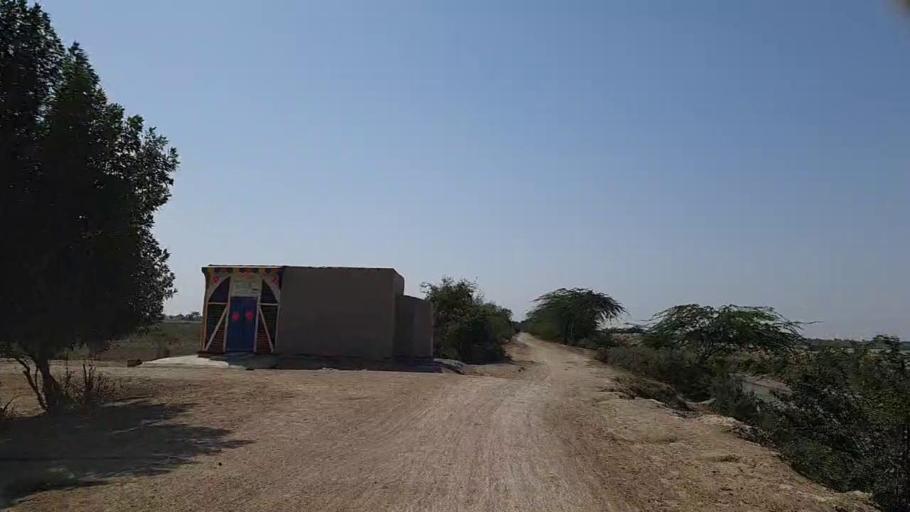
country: PK
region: Sindh
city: Mirpur Batoro
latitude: 24.6714
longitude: 68.3058
